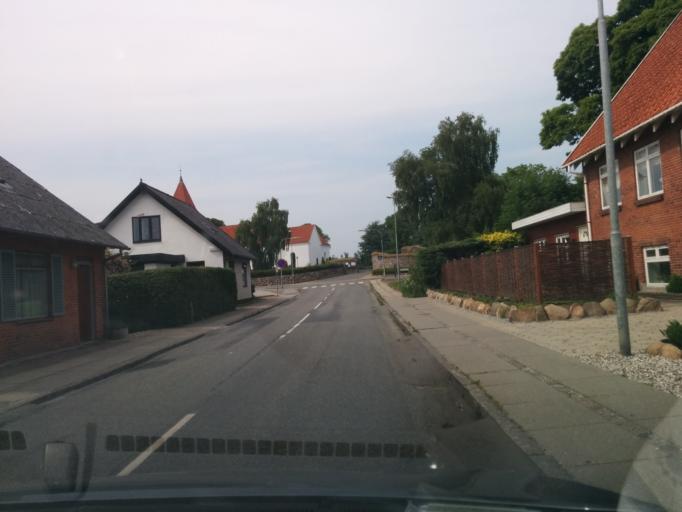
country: DK
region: Central Jutland
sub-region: Arhus Kommune
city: Malling
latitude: 56.0386
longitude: 10.1954
